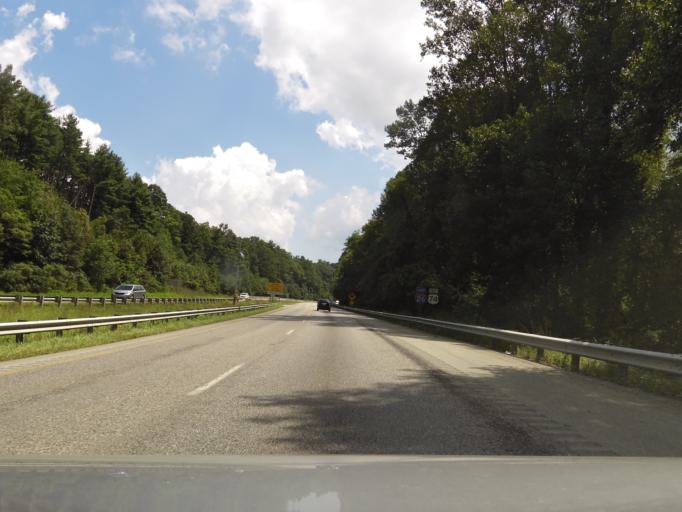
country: US
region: North Carolina
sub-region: Henderson County
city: East Flat Rock
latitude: 35.2781
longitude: -82.3940
